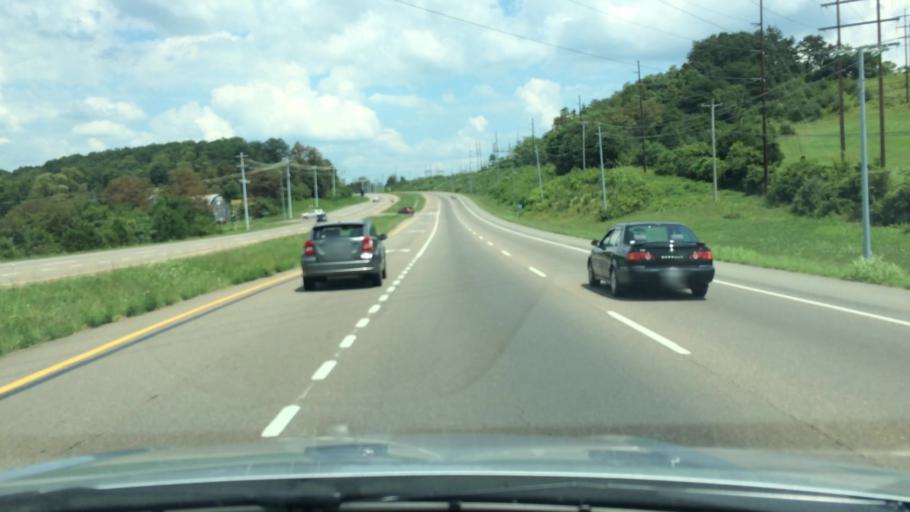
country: US
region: Tennessee
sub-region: Hamblen County
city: Morristown
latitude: 36.1876
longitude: -83.2979
